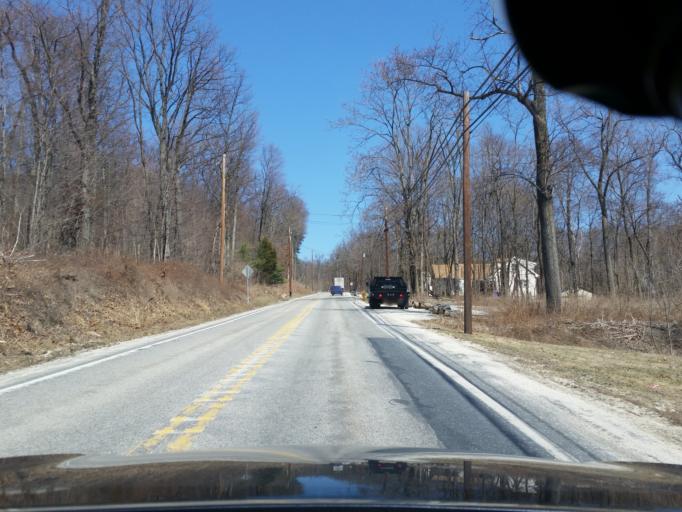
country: US
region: Pennsylvania
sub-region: Cumberland County
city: Schlusser
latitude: 40.2861
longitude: -77.1409
